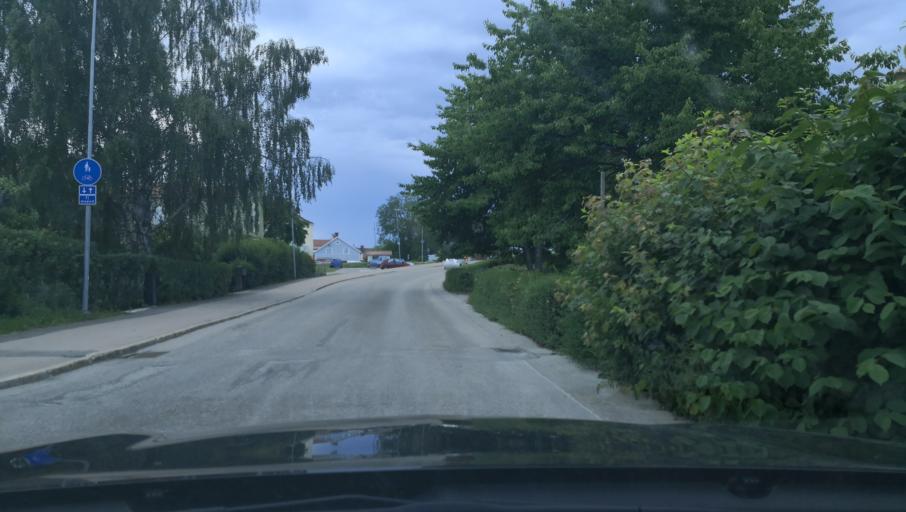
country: SE
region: Vaestmanland
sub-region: Fagersta Kommun
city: Fagersta
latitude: 59.9881
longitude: 15.8225
